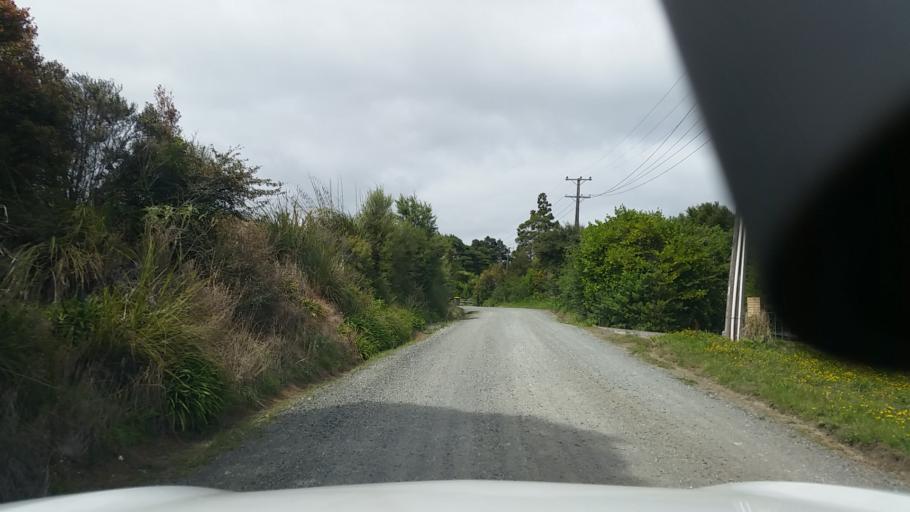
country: NZ
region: Auckland
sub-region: Auckland
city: Muriwai Beach
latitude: -36.8456
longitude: 174.5231
